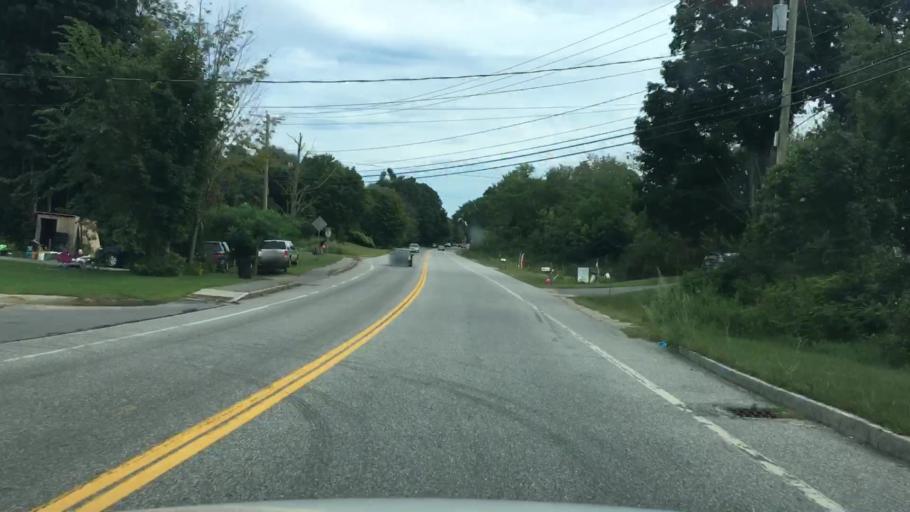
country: US
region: New Hampshire
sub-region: Strafford County
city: Dover
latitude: 43.1861
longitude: -70.8963
